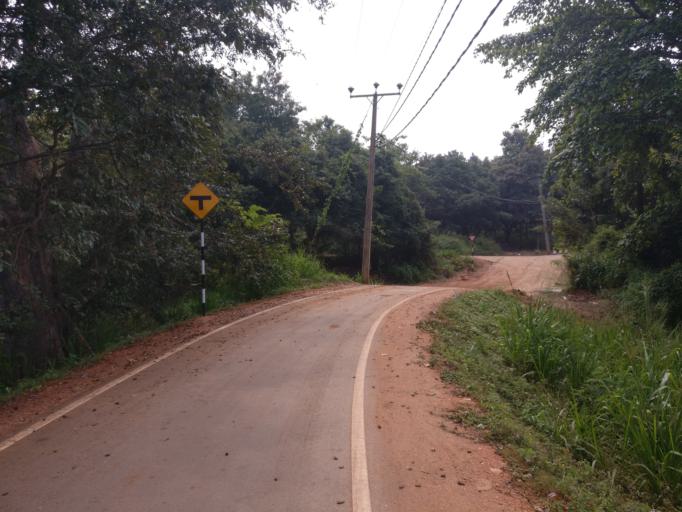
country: LK
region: Central
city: Dambulla
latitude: 7.8357
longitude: 80.6482
